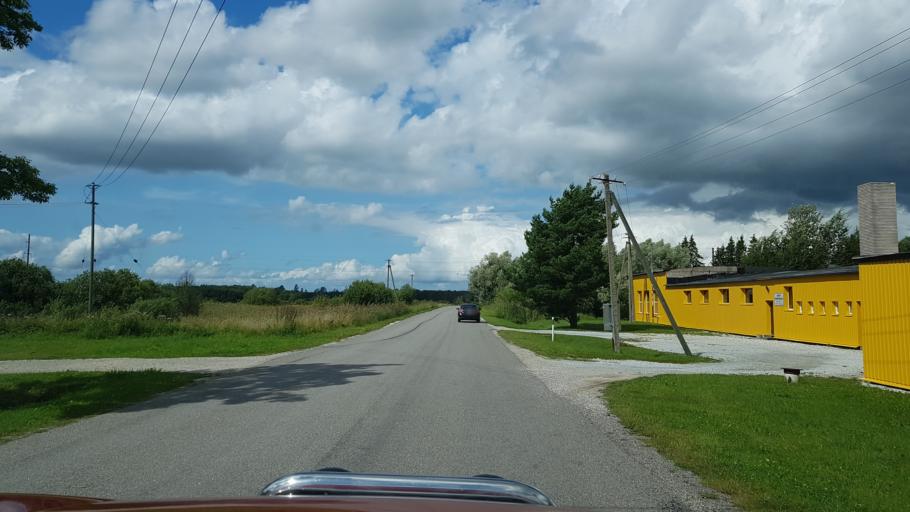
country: EE
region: Laeaene
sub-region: Lihula vald
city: Lihula
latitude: 58.6933
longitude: 23.8345
